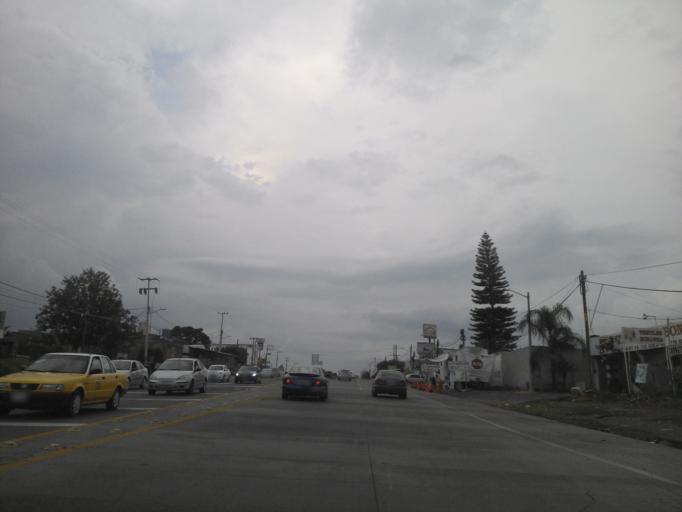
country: MX
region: Jalisco
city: Zapotlanejo
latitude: 20.6154
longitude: -103.0799
